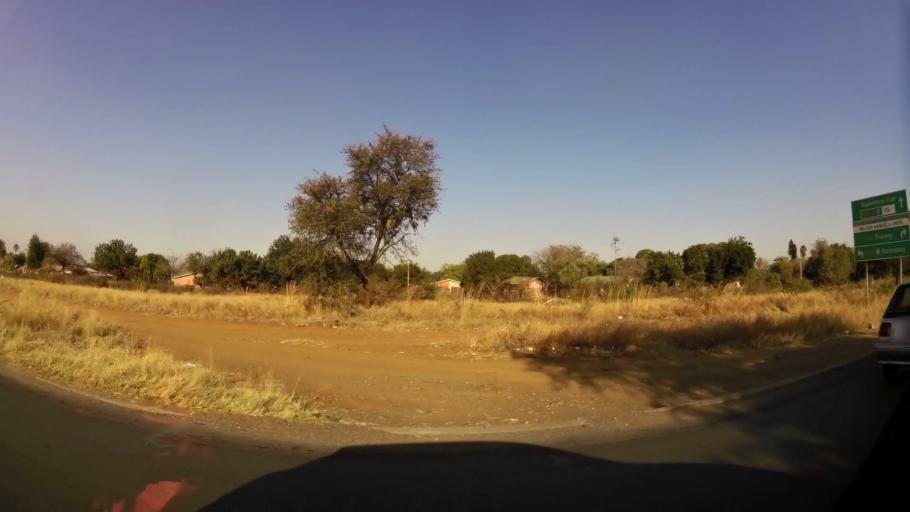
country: ZA
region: North-West
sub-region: Bojanala Platinum District Municipality
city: Rustenburg
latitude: -25.6526
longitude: 27.2214
